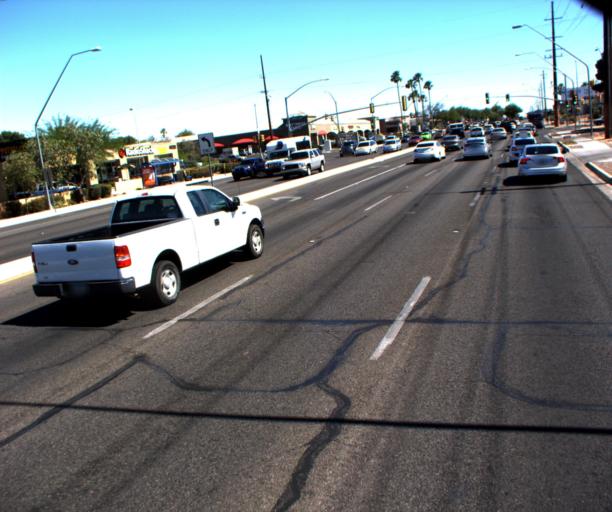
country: US
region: Arizona
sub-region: Pima County
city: Flowing Wells
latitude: 32.2802
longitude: -110.9783
